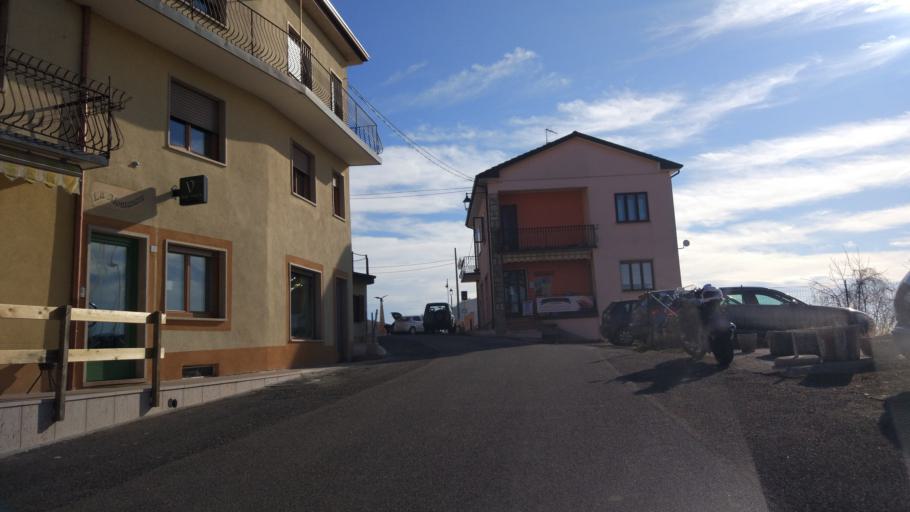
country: IT
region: Veneto
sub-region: Provincia di Verona
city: Selva di Progno
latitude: 45.6377
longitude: 11.1540
